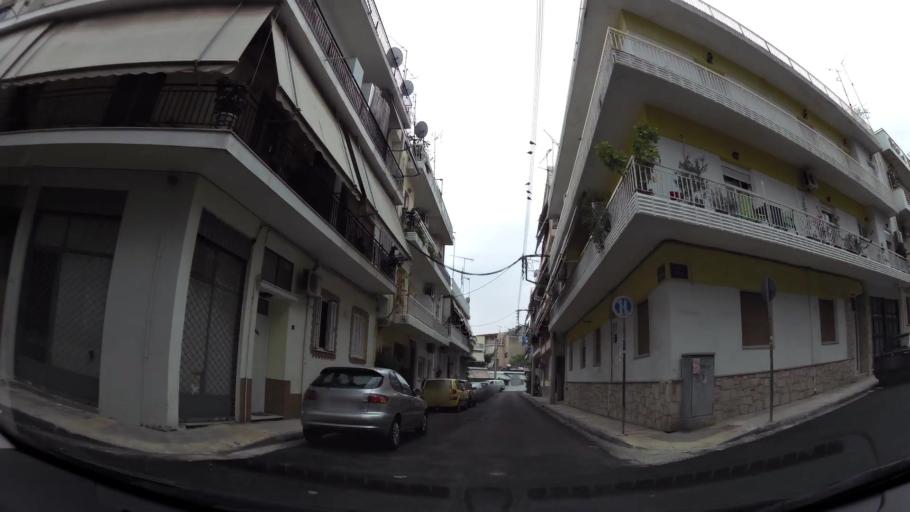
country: GR
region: Attica
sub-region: Nomarchia Athinas
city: Aigaleo
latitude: 37.9825
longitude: 23.6742
